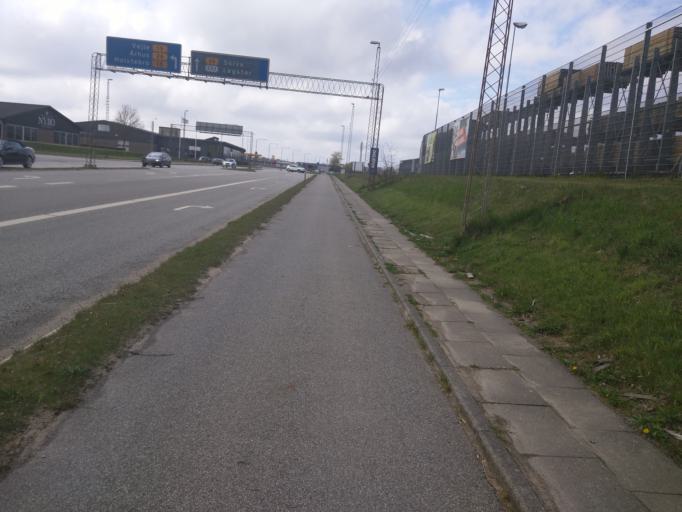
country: DK
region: Central Jutland
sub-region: Viborg Kommune
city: Viborg
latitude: 56.4686
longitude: 9.4130
